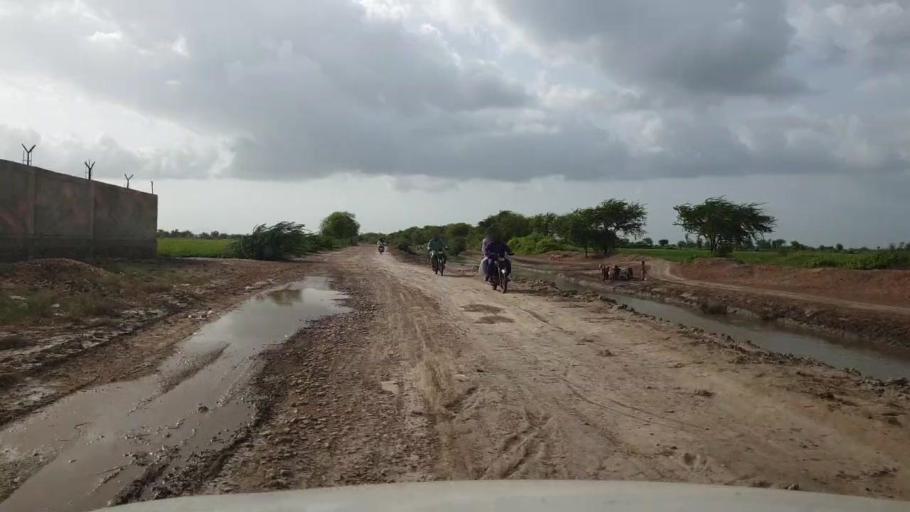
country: PK
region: Sindh
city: Kario
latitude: 24.7853
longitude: 68.5850
